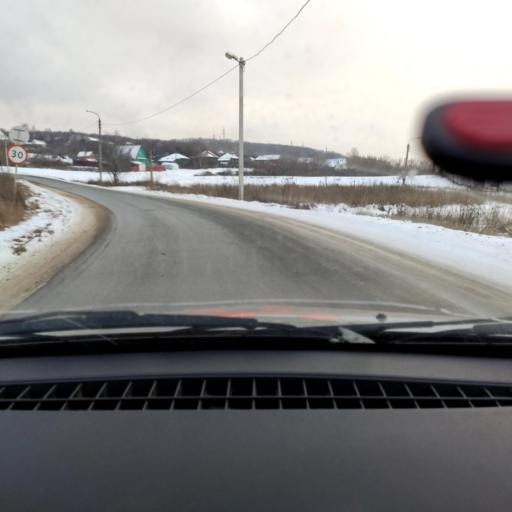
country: RU
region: Bashkortostan
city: Blagoveshchensk
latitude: 54.8893
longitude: 56.0362
